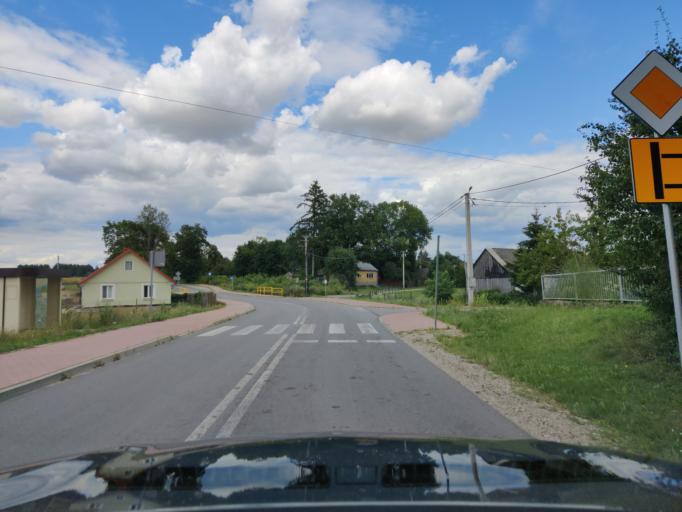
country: PL
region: Masovian Voivodeship
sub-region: Powiat wegrowski
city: Miedzna
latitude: 52.5383
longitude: 22.0894
